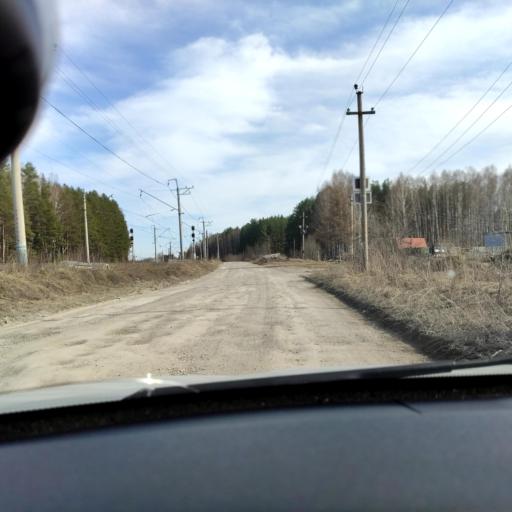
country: RU
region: Perm
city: Overyata
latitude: 58.0570
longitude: 55.9925
